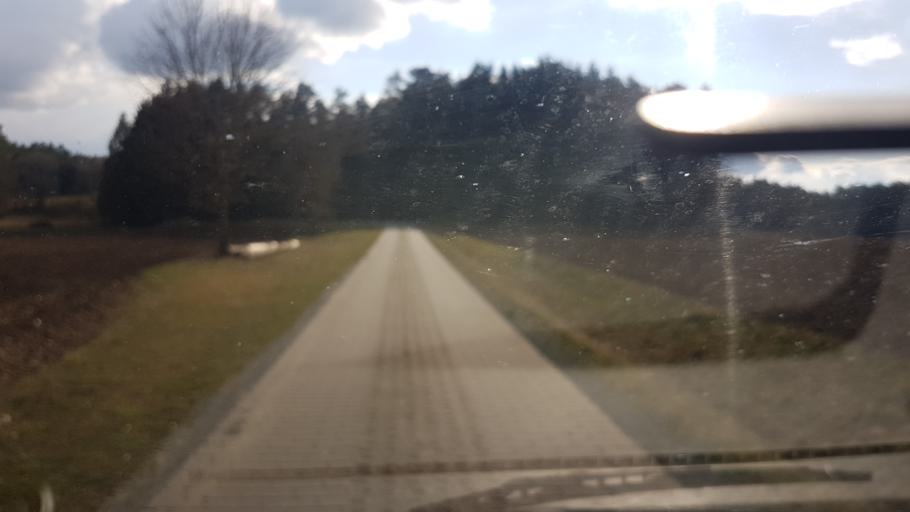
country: DE
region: Bavaria
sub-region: Upper Franconia
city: Stadelhofen
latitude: 50.0019
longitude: 11.2349
